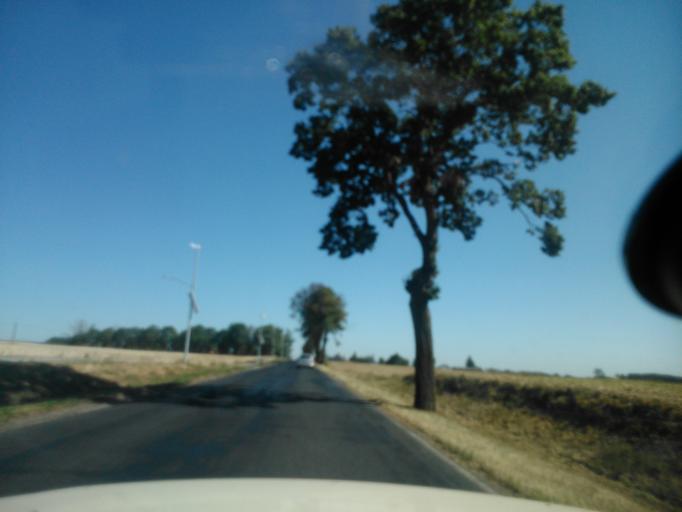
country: PL
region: Kujawsko-Pomorskie
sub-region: Powiat golubsko-dobrzynski
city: Kowalewo Pomorskie
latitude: 53.1550
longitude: 18.9412
